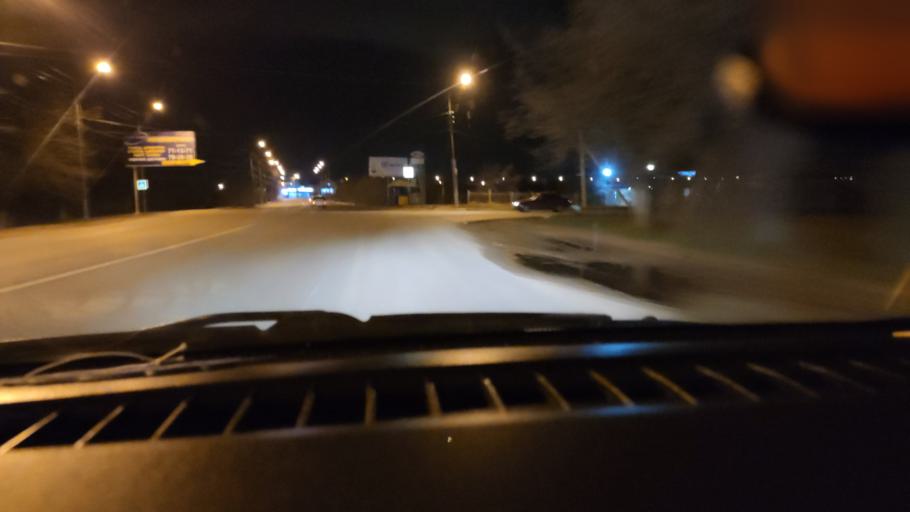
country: RU
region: Saratov
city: Privolzhskiy
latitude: 51.4224
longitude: 46.0472
